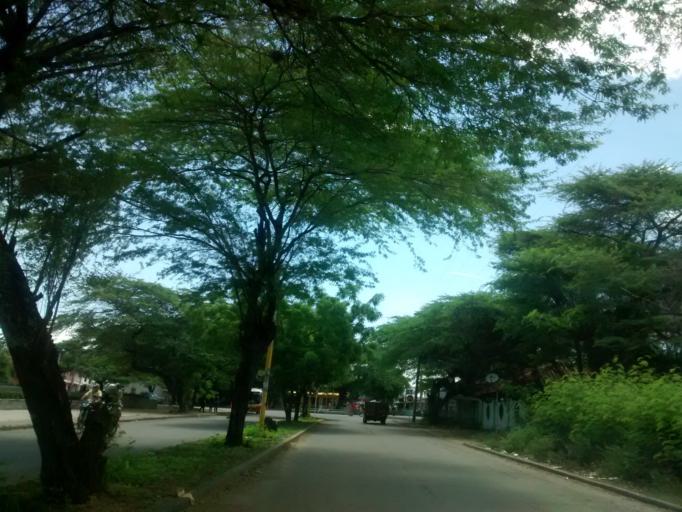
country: CO
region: Cundinamarca
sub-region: Girardot
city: Girardot City
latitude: 4.3099
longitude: -74.7920
